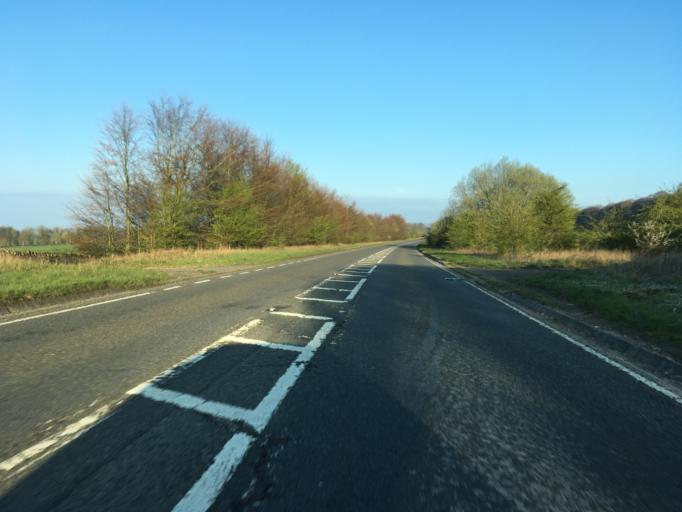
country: GB
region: England
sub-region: Gloucestershire
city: Westfield
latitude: 51.8463
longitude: -1.8766
